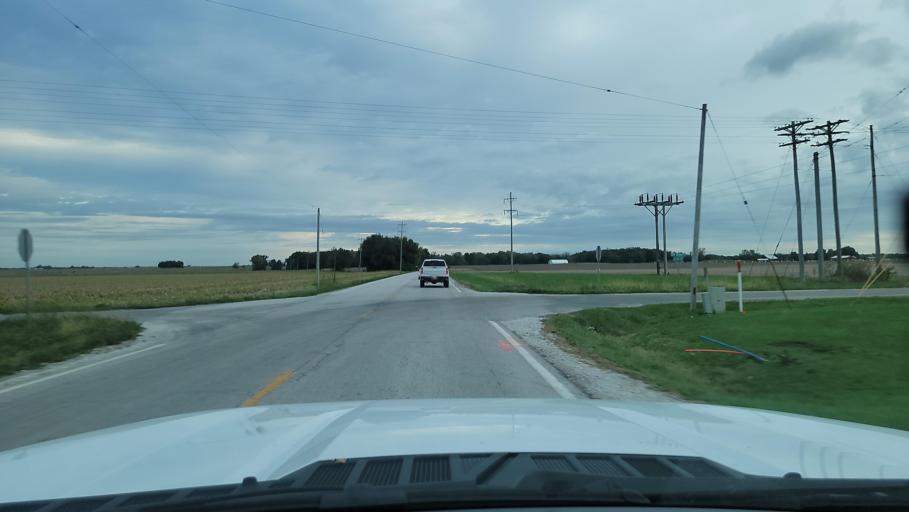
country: US
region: Illinois
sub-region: Schuyler County
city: Rushville
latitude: 40.1458
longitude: -90.5578
